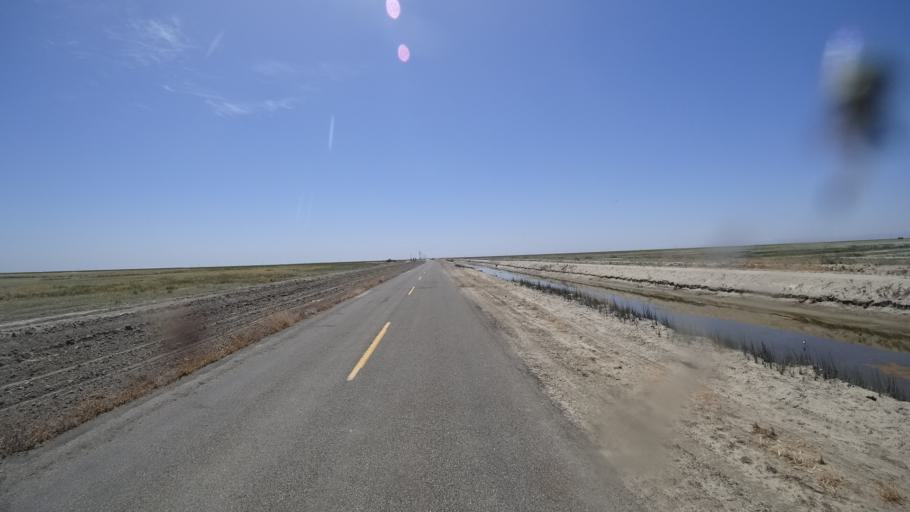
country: US
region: California
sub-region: Kings County
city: Corcoran
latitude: 36.1265
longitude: -119.6802
